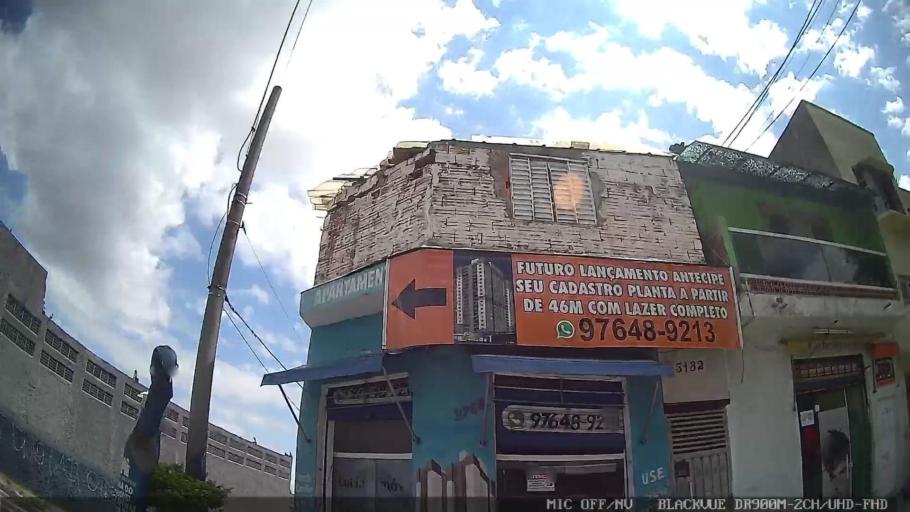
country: BR
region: Sao Paulo
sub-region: Ferraz De Vasconcelos
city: Ferraz de Vasconcelos
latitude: -23.5214
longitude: -46.4438
